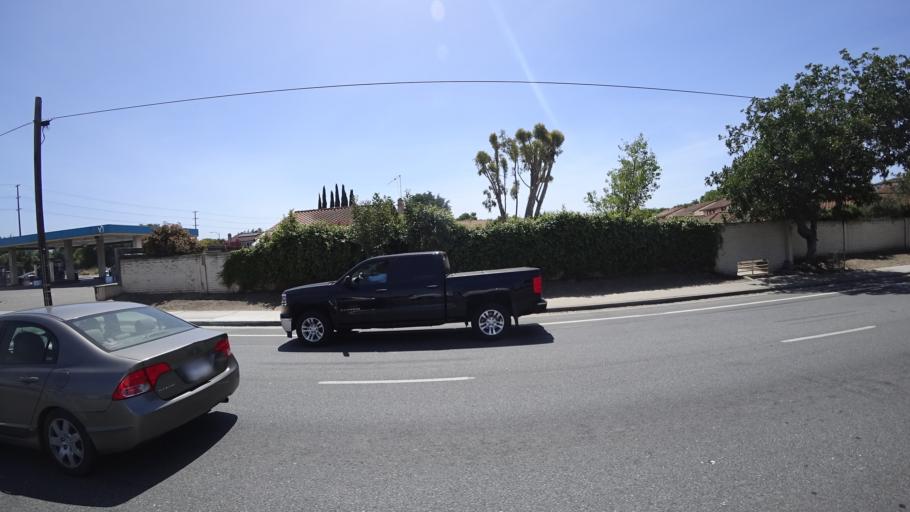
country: US
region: California
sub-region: Santa Clara County
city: Seven Trees
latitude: 37.3074
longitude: -121.8484
